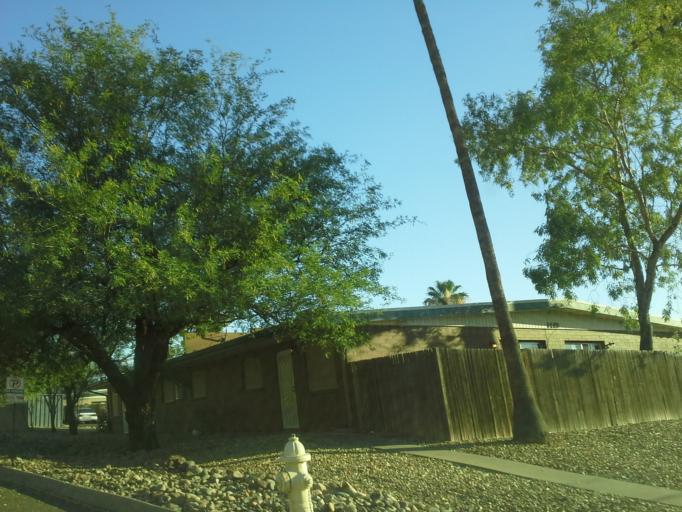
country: US
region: Arizona
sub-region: Maricopa County
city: Paradise Valley
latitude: 33.5677
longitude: -112.0514
